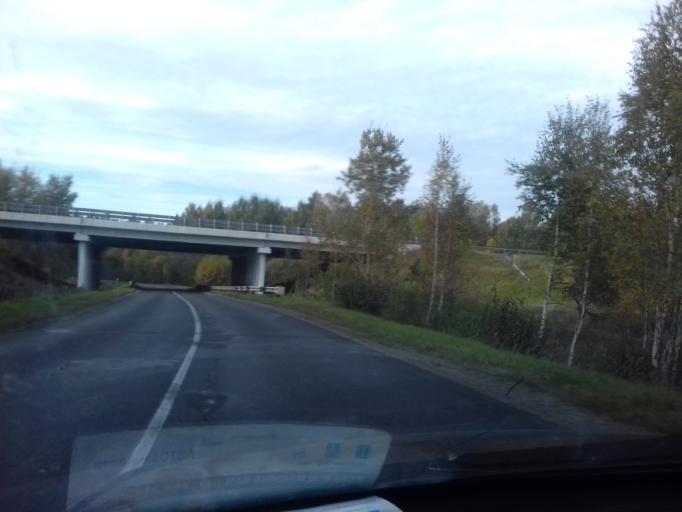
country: BY
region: Minsk
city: Hatava
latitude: 53.7571
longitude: 27.6622
